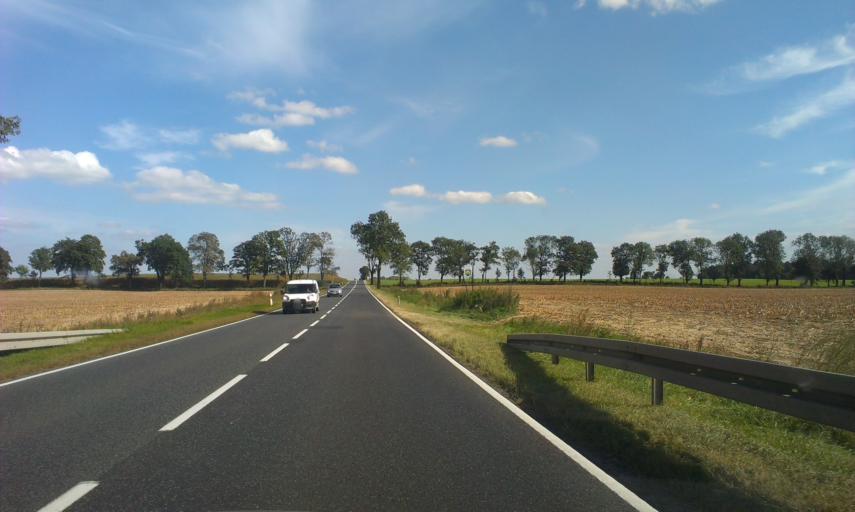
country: PL
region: Greater Poland Voivodeship
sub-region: Powiat pilski
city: Osiek nad Notecia
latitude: 53.1549
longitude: 17.3553
